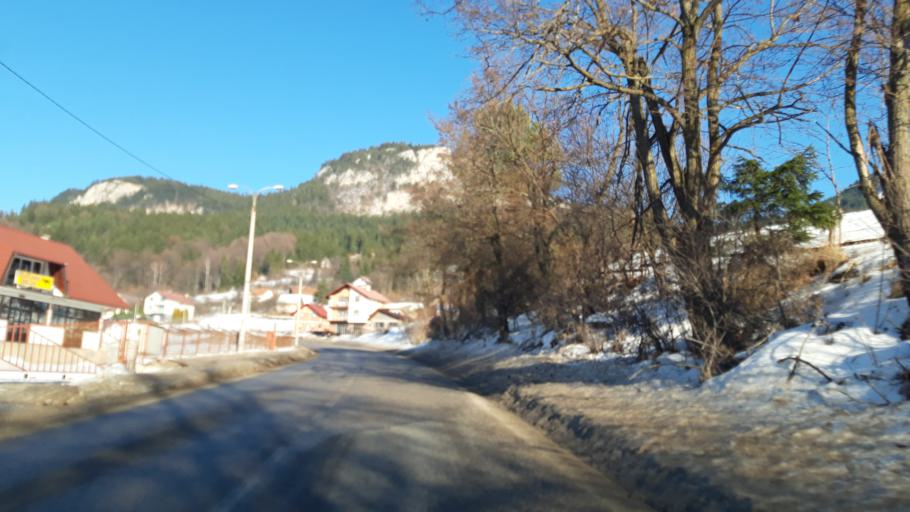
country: BA
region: Republika Srpska
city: Pale
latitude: 43.8933
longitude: 18.6349
